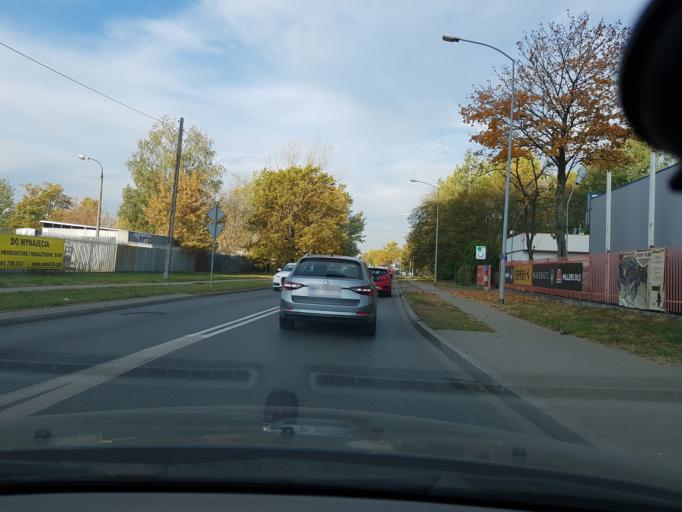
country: PL
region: Masovian Voivodeship
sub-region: Warszawa
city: Bielany
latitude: 52.2834
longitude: 20.9138
